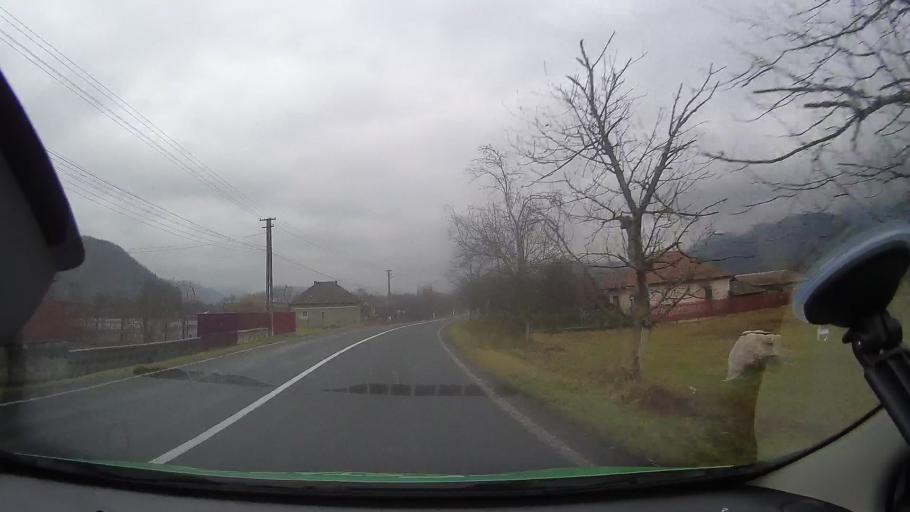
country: RO
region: Arad
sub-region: Comuna Plescuta
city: Plescuta
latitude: 46.2930
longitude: 22.3988
